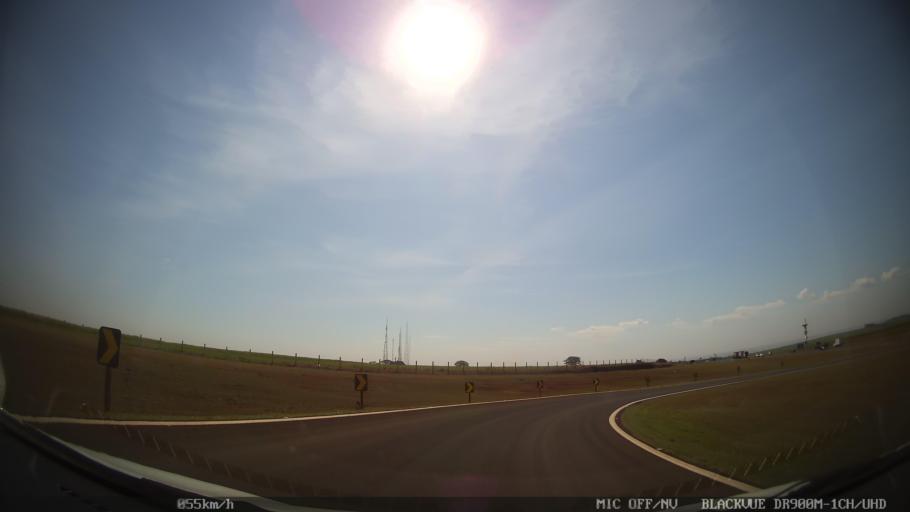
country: BR
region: Sao Paulo
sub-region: Ribeirao Preto
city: Ribeirao Preto
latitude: -21.1662
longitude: -47.9007
